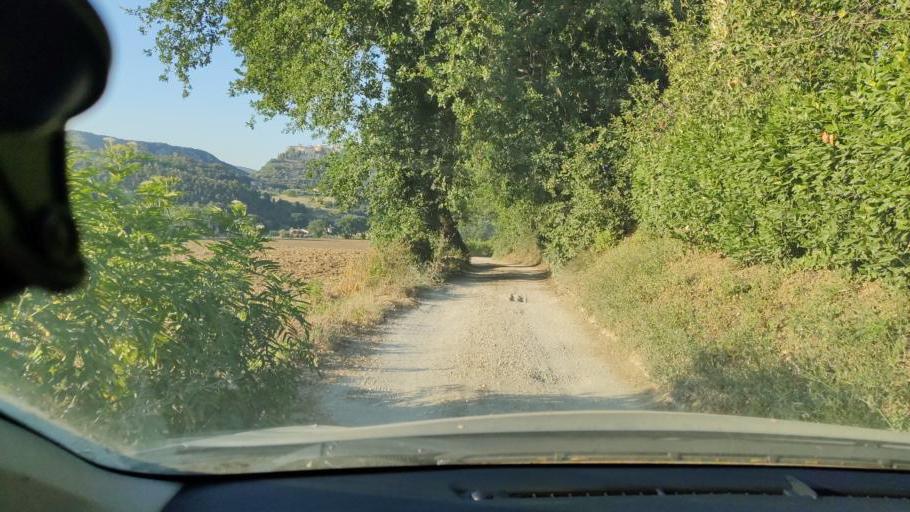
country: IT
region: Umbria
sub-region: Provincia di Terni
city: Amelia
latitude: 42.5452
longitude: 12.4039
